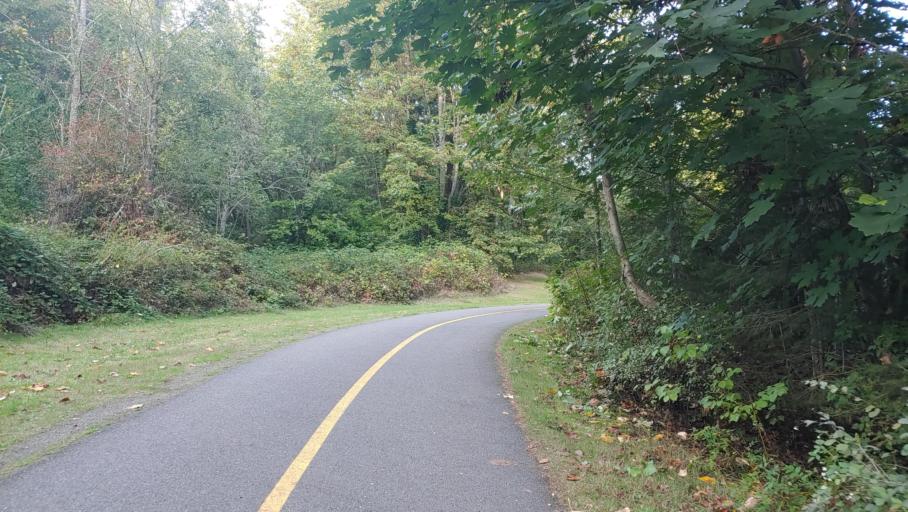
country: US
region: Washington
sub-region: King County
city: Des Moines
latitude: 47.4210
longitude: -122.3067
